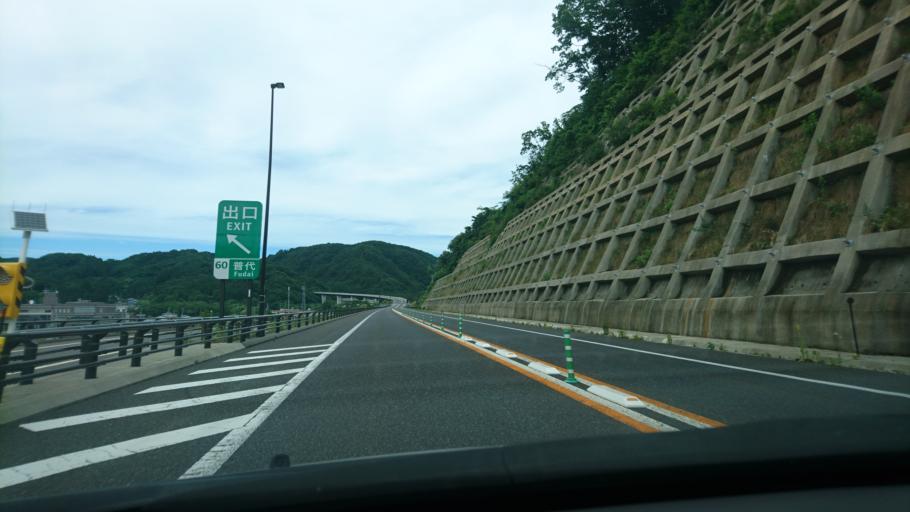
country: JP
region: Iwate
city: Miyako
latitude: 40.0016
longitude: 141.8866
